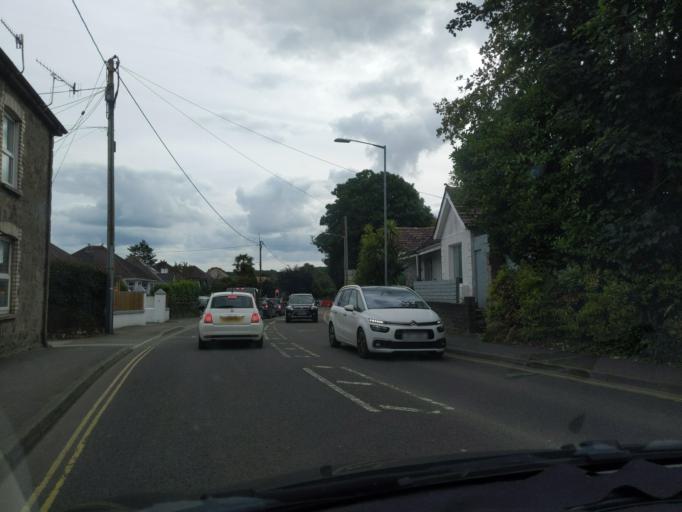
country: GB
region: England
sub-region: Cornwall
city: St Austell
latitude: 50.3330
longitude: -4.7930
